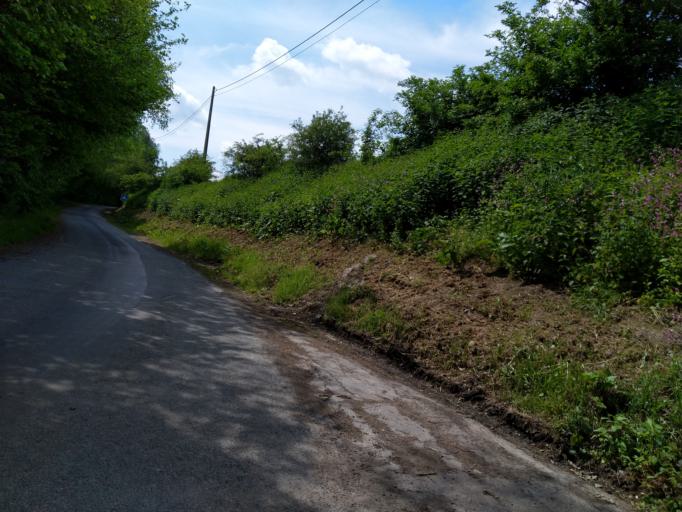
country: FR
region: Nord-Pas-de-Calais
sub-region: Departement du Nord
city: Le Quesnoy
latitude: 50.2608
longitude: 3.6485
